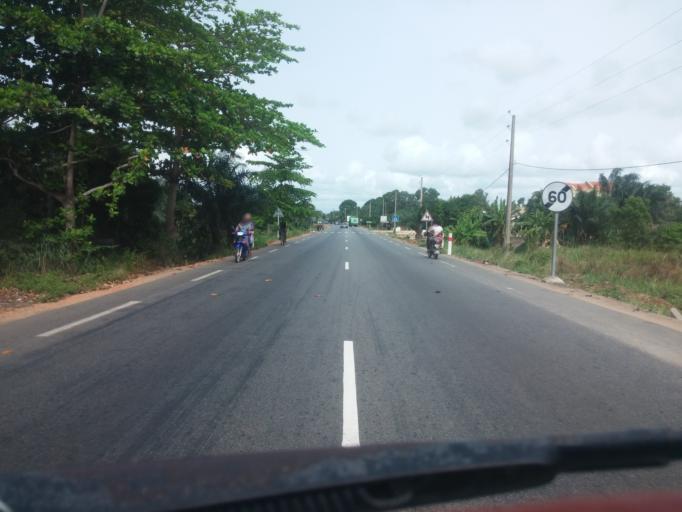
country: BJ
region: Mono
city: Come
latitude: 6.4002
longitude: 1.9196
